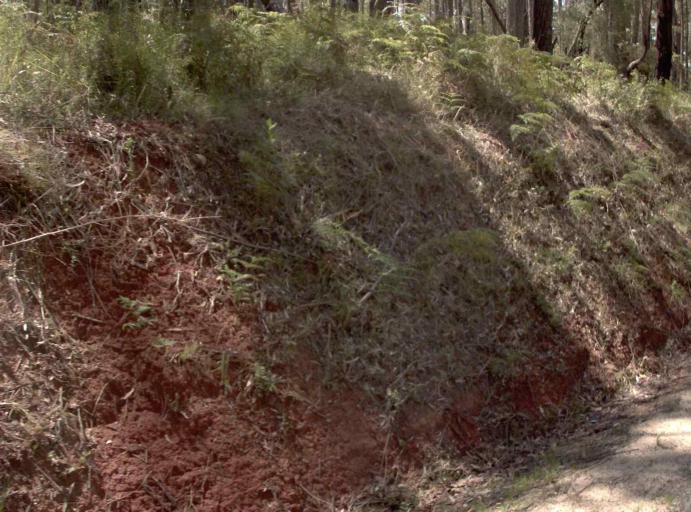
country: AU
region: New South Wales
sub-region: Bombala
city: Bombala
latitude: -37.5787
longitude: 149.0150
